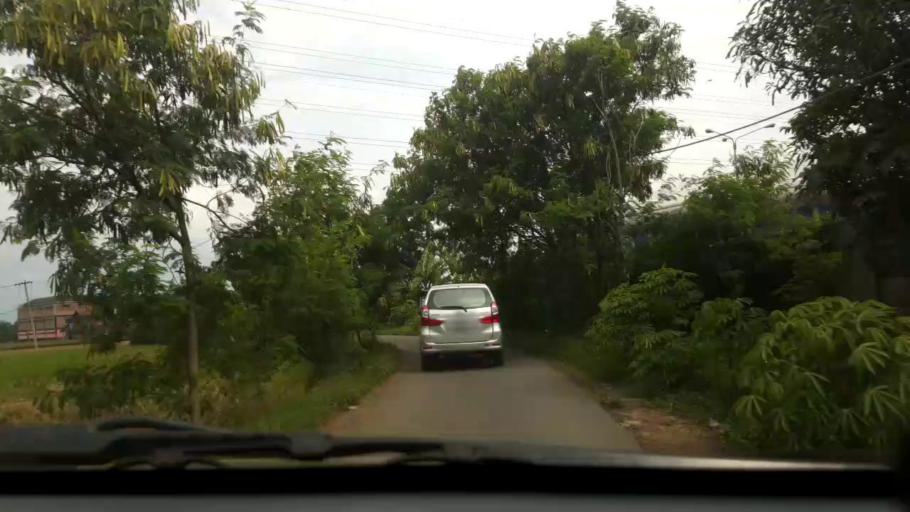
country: ID
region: West Java
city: Cileunyi
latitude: -6.9541
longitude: 107.7126
